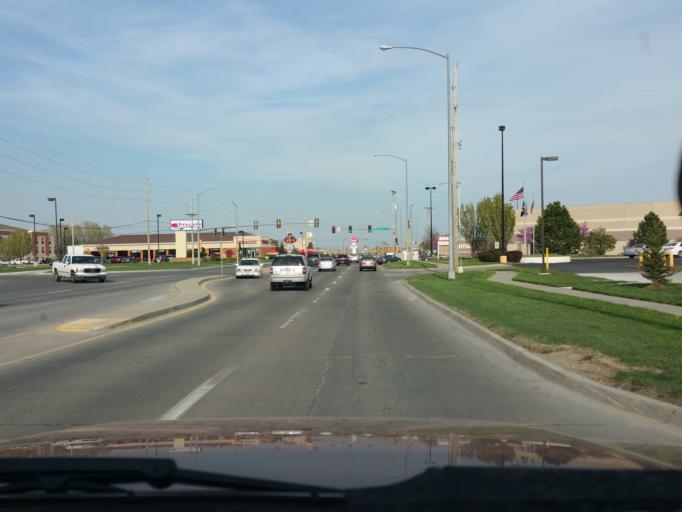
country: US
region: Kansas
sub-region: Riley County
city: Manhattan
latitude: 39.1892
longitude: -96.5586
